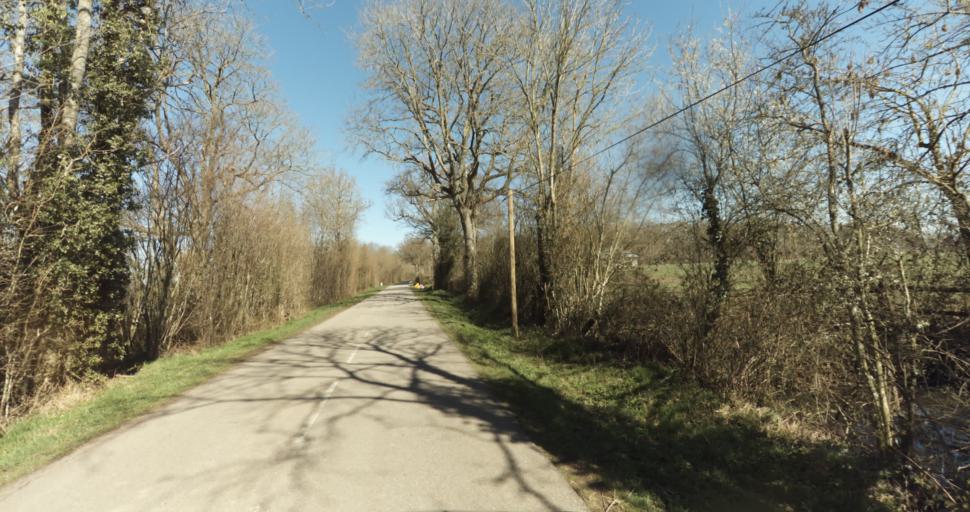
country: FR
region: Lower Normandy
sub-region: Departement de l'Orne
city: Trun
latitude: 48.9218
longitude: 0.0646
